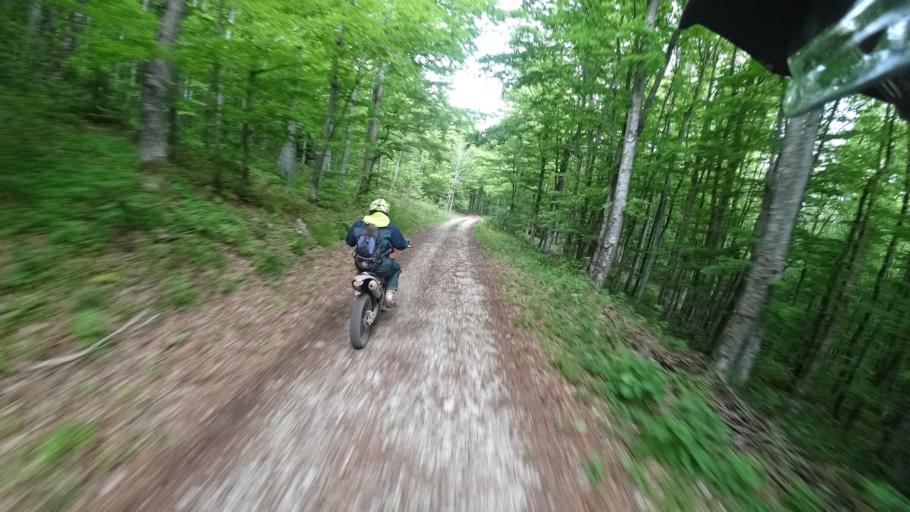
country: HR
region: Karlovacka
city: Plaski
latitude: 45.0110
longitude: 15.3225
